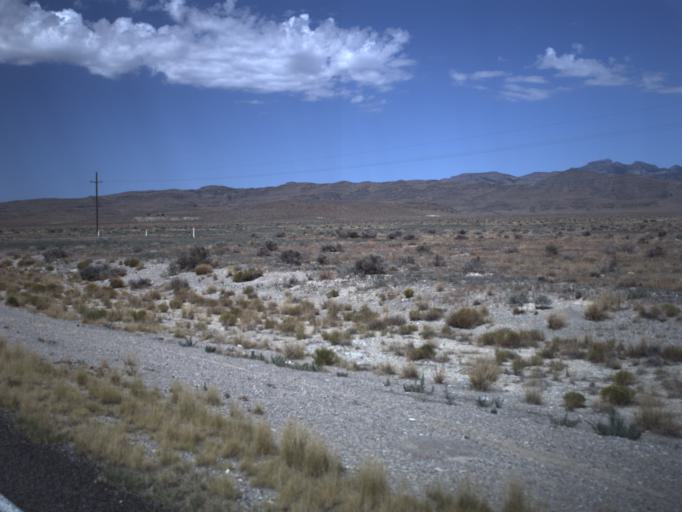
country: US
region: Utah
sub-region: Millard County
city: Delta
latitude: 39.0723
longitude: -113.2172
